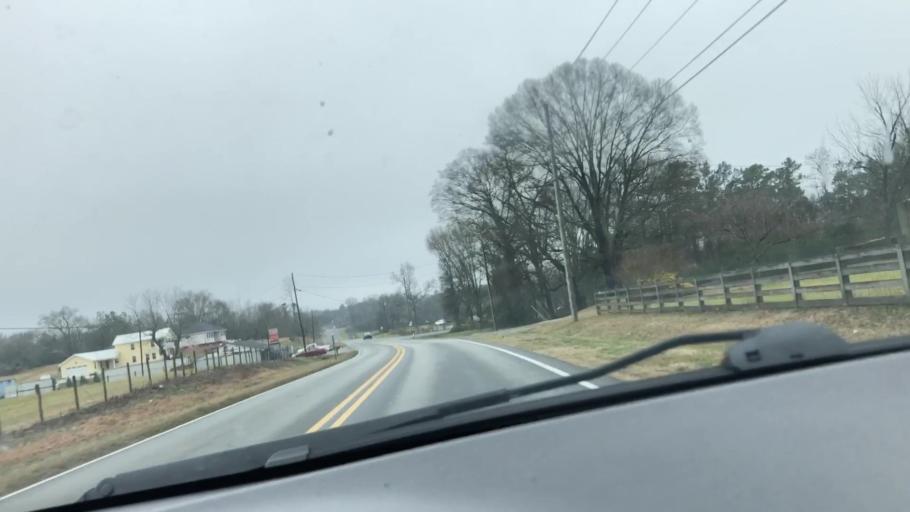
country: US
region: Georgia
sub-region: Bartow County
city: Cartersville
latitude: 34.1964
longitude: -84.8362
